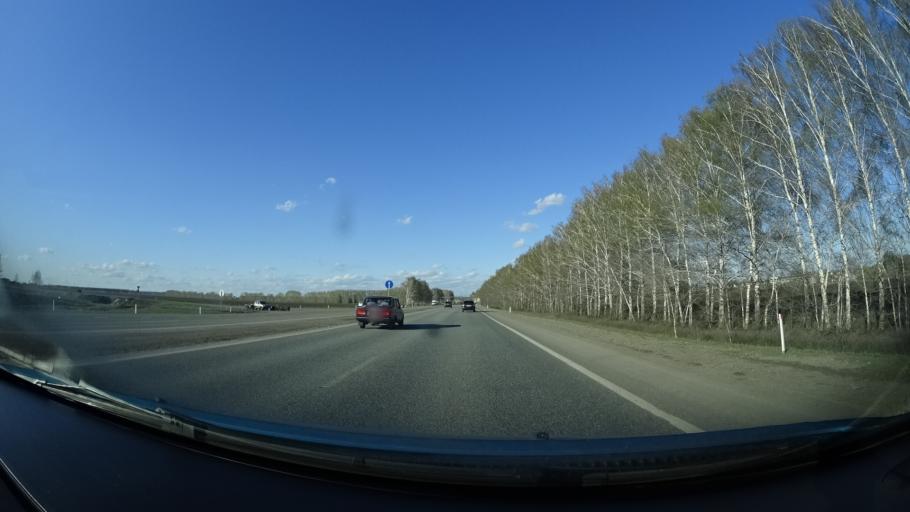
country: RU
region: Bashkortostan
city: Ufa
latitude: 54.5429
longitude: 55.9149
